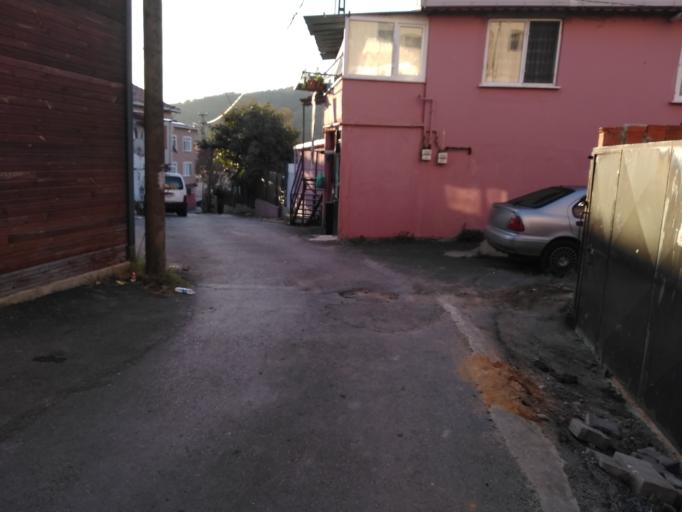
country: TR
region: Istanbul
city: Arikoey
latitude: 41.2362
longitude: 28.9839
